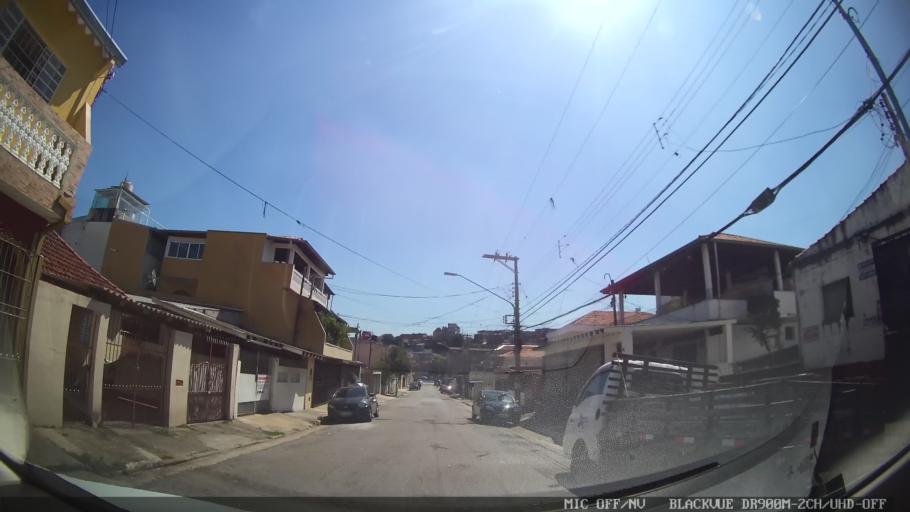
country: BR
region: Sao Paulo
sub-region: Sao Paulo
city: Sao Paulo
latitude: -23.4942
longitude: -46.6572
